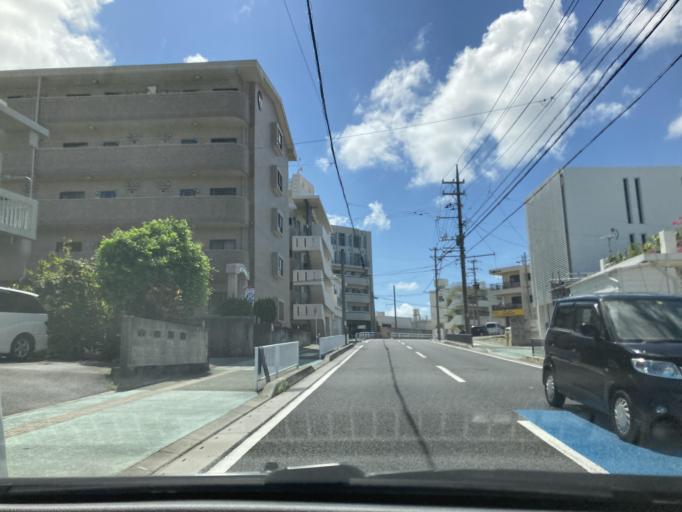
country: JP
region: Okinawa
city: Tomigusuku
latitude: 26.1973
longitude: 127.6720
